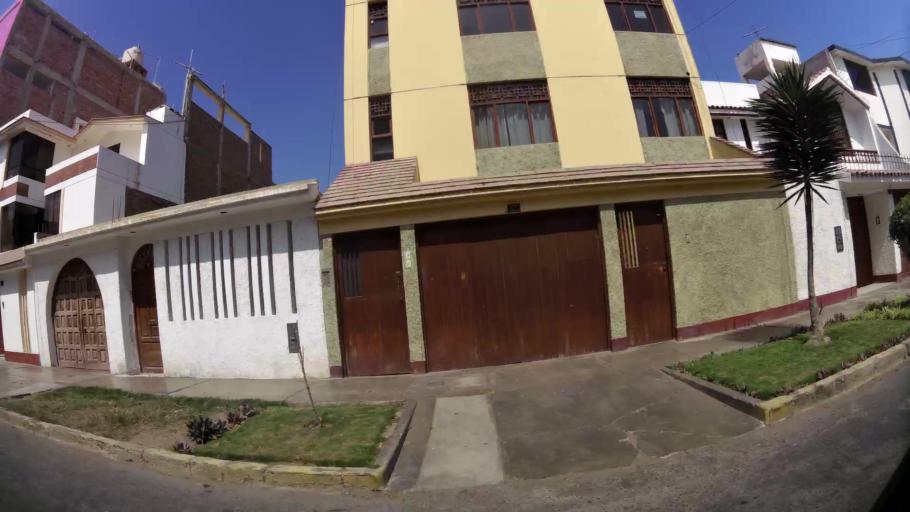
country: PE
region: La Libertad
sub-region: Provincia de Trujillo
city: Buenos Aires
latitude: -8.1266
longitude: -79.0397
